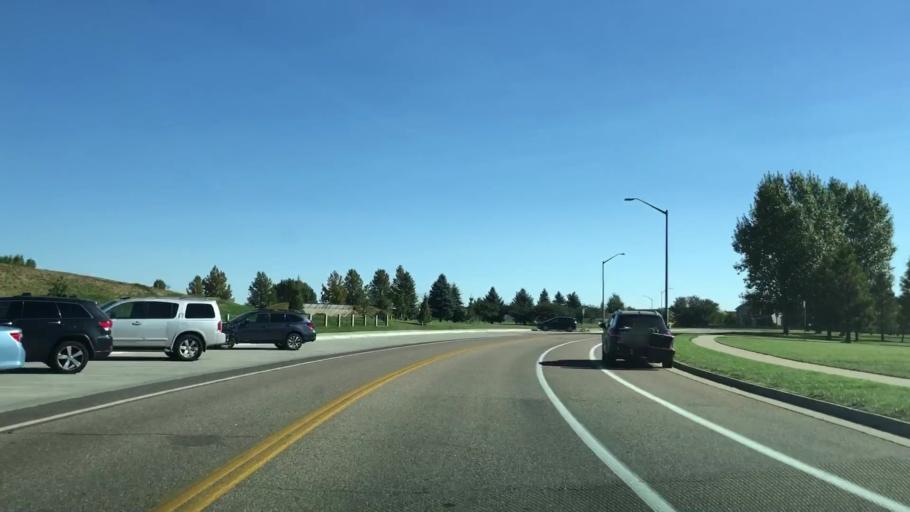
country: US
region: Colorado
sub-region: Larimer County
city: Fort Collins
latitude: 40.5100
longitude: -105.0130
